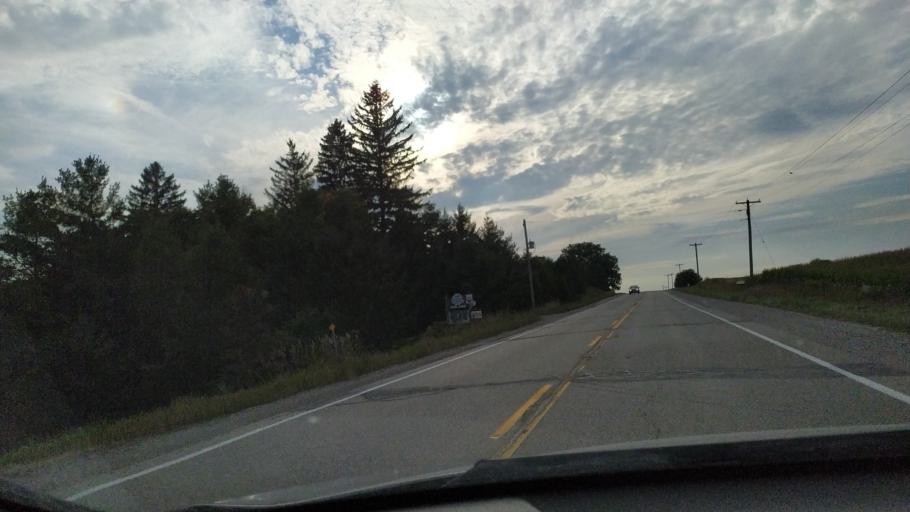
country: CA
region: Ontario
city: Stratford
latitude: 43.4250
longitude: -80.8502
